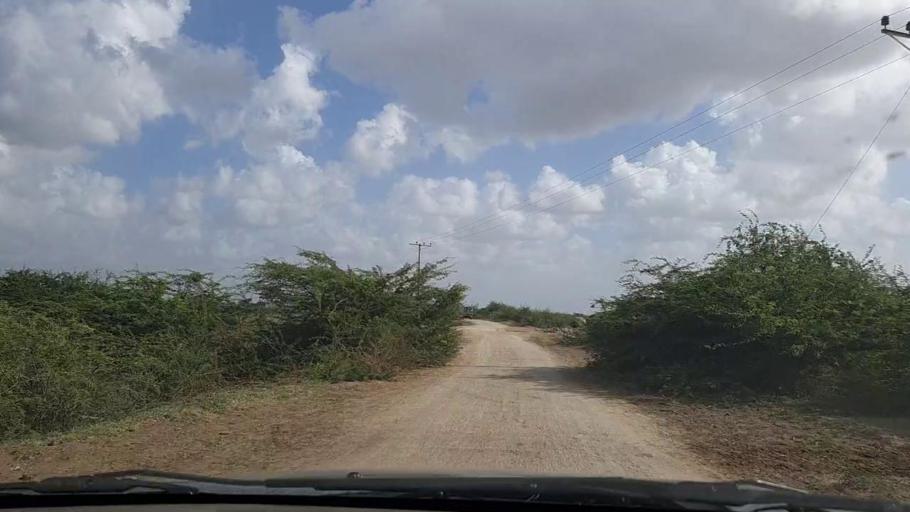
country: PK
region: Sindh
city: Keti Bandar
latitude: 24.0945
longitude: 67.6115
